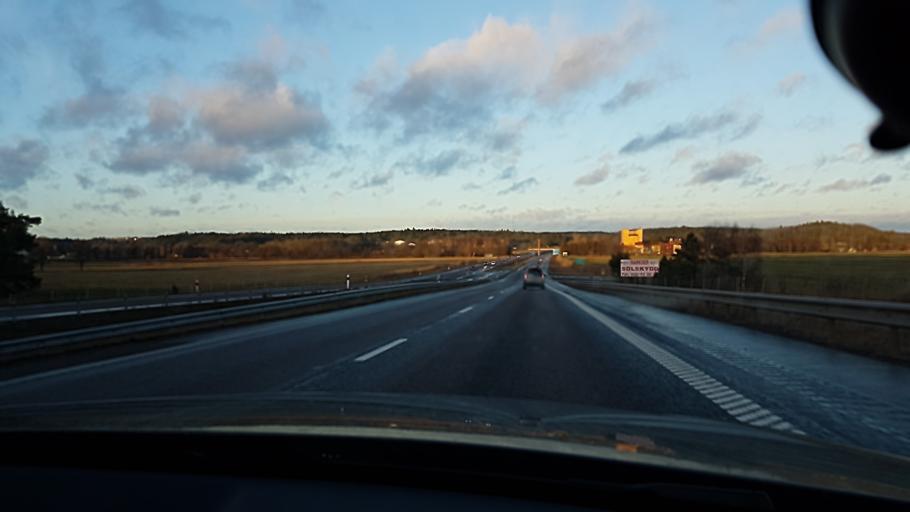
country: SE
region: Stockholm
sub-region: Sodertalje Kommun
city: Pershagen
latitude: 59.0750
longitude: 17.5931
